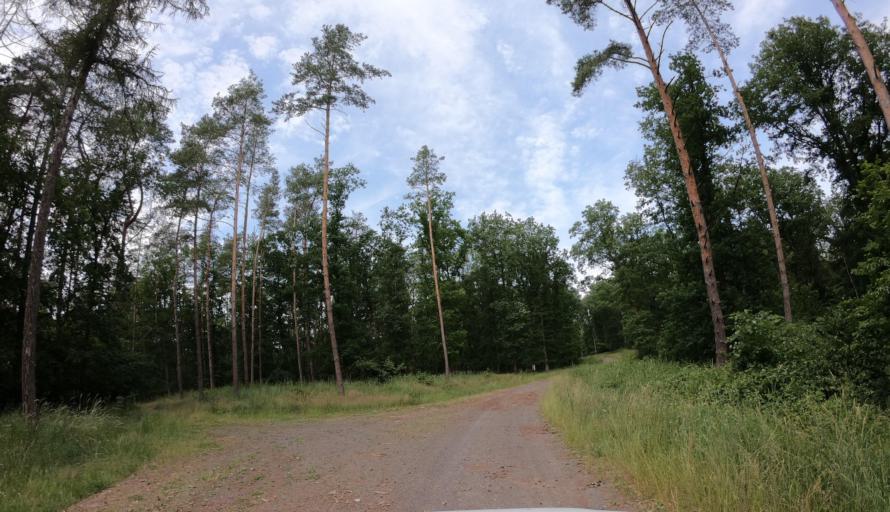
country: PL
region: West Pomeranian Voivodeship
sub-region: Powiat gryfinski
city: Banie
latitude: 53.0271
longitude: 14.7423
